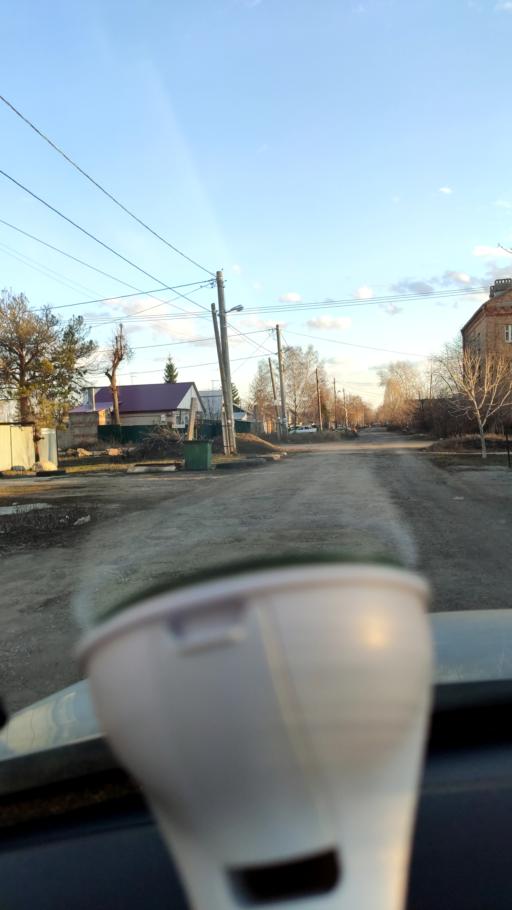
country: RU
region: Samara
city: Smyshlyayevka
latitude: 53.2495
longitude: 50.3430
